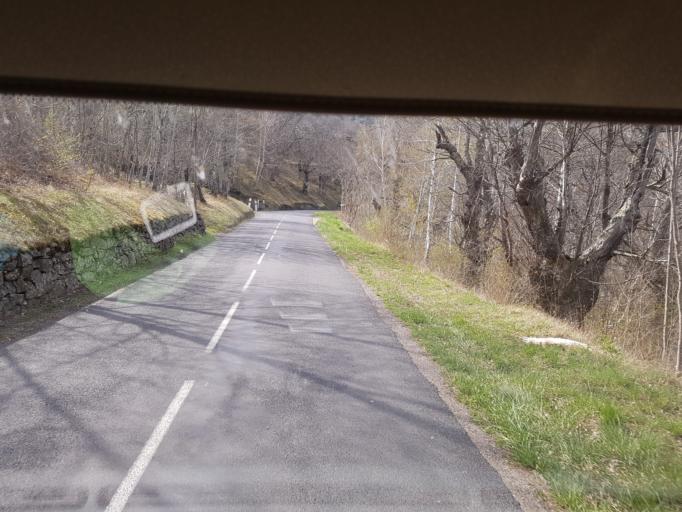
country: FR
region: Languedoc-Roussillon
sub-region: Departement de la Lozere
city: Florac
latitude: 44.2750
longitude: 3.5901
